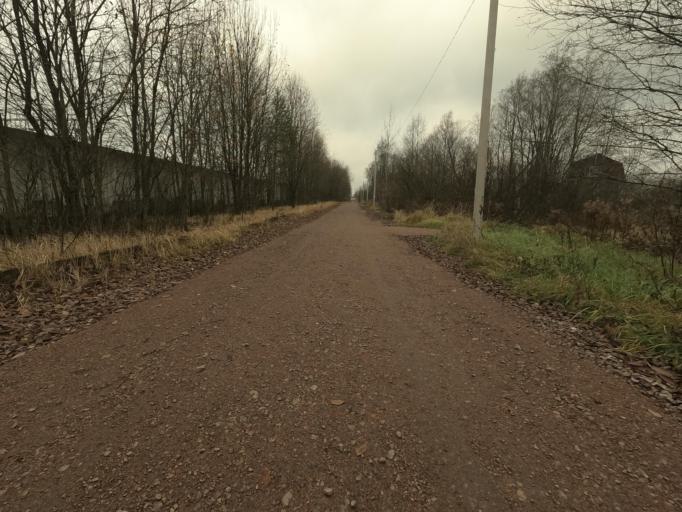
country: RU
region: Leningrad
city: Lyuban'
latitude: 59.4899
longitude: 31.2696
